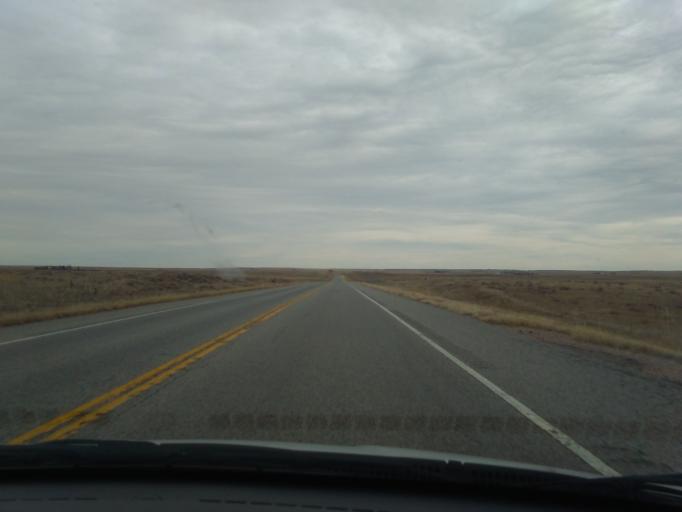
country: US
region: Colorado
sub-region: Washington County
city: Akron
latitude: 40.2184
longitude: -103.3685
